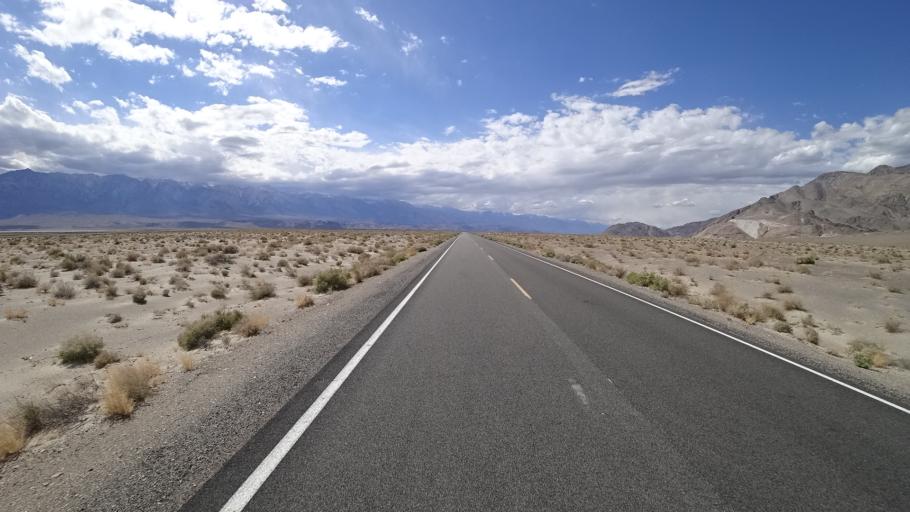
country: US
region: California
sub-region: Inyo County
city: Lone Pine
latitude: 36.5496
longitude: -117.9482
